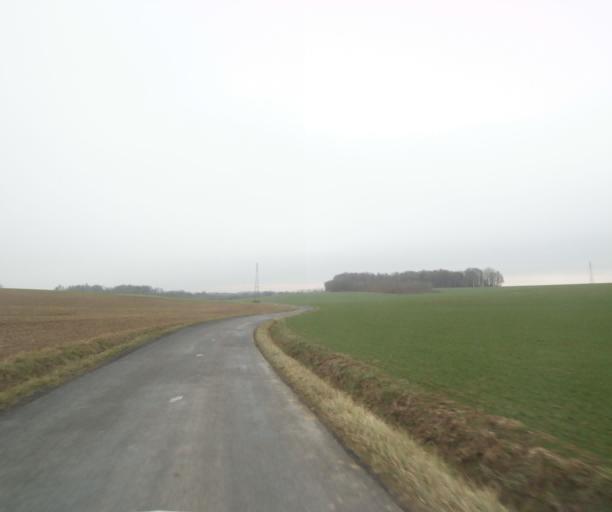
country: FR
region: Champagne-Ardenne
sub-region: Departement de la Haute-Marne
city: Bienville
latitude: 48.5737
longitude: 5.0240
